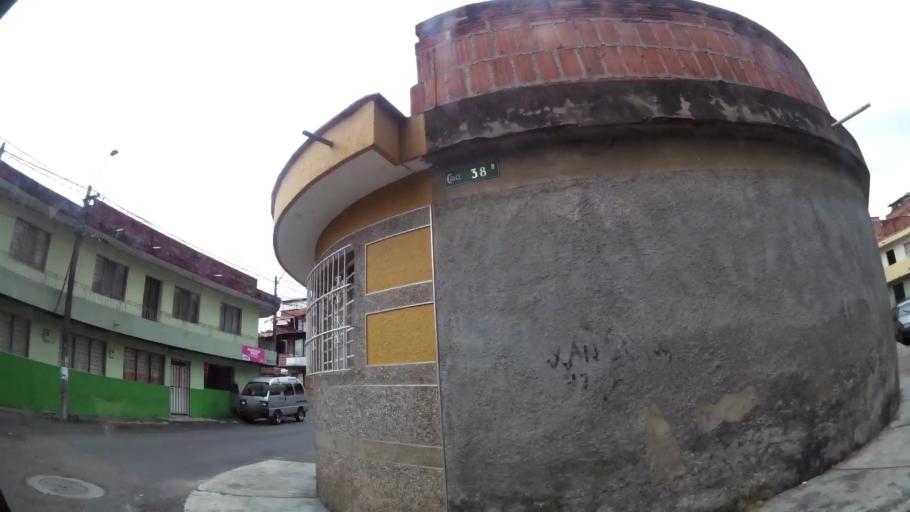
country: CO
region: Antioquia
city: Medellin
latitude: 6.2357
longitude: -75.5590
